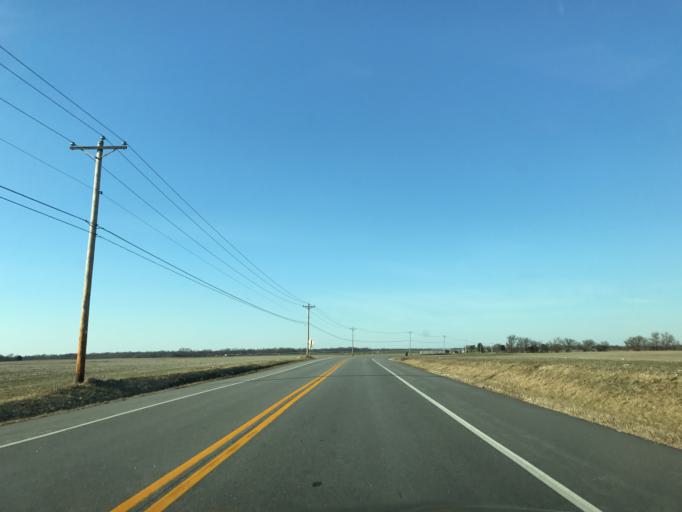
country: US
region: Maryland
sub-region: Queen Anne's County
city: Kingstown
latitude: 39.2043
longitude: -75.8635
